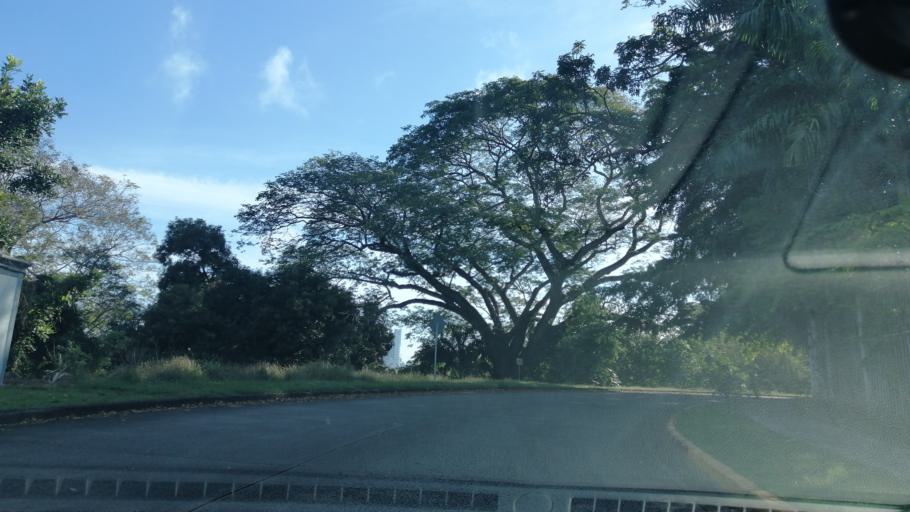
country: PA
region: Panama
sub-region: Distrito de Panama
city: Ancon
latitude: 8.9644
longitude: -79.5514
